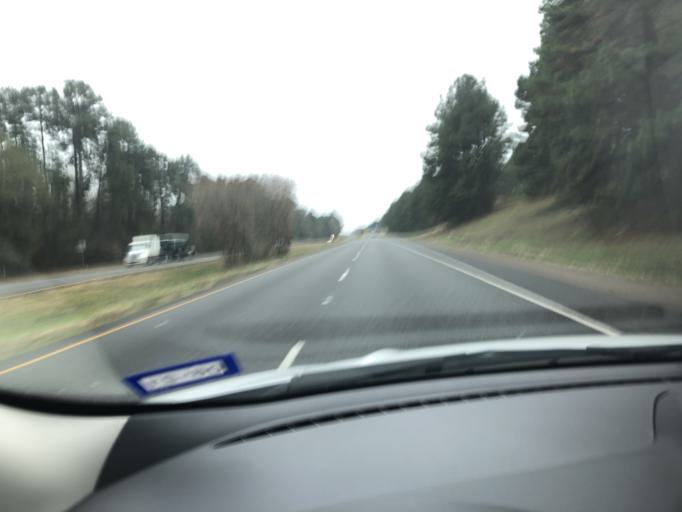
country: US
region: Texas
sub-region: Nacogdoches County
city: Nacogdoches
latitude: 31.5442
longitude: -94.6901
